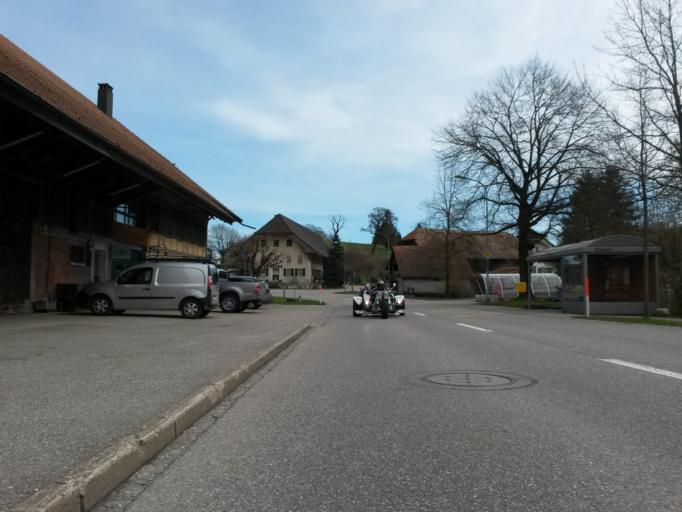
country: CH
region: Solothurn
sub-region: Bezirk Lebern
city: Langendorf
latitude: 47.1903
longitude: 7.5014
